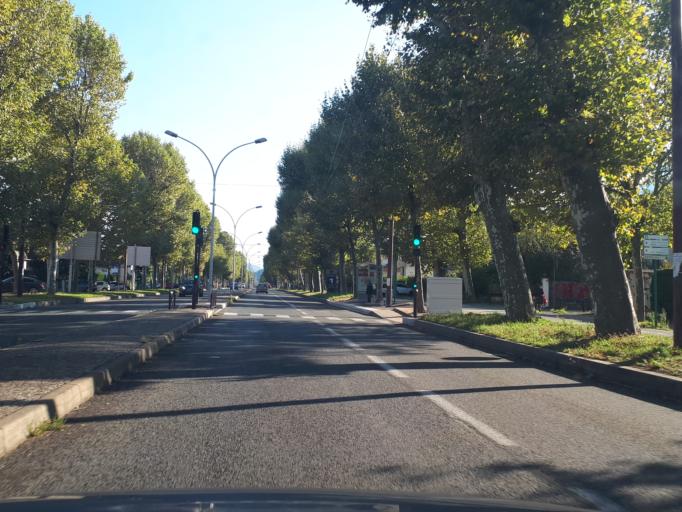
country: FR
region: Rhone-Alpes
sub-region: Departement de l'Isere
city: Grenoble
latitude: 45.1565
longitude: 5.7084
